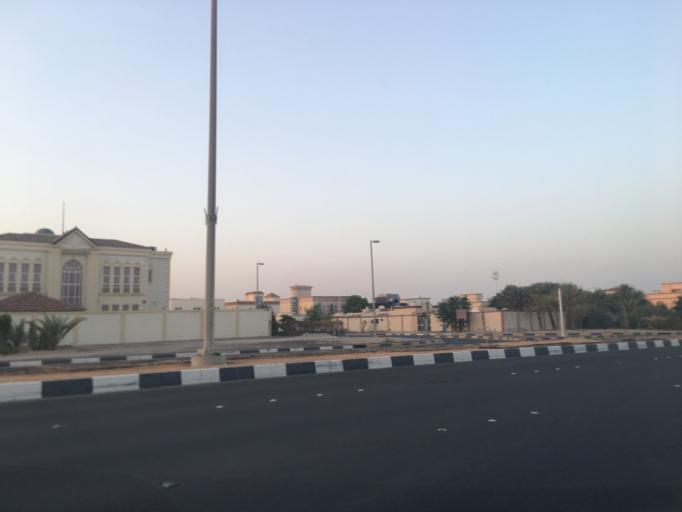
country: AE
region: Abu Dhabi
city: Abu Dhabi
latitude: 24.3047
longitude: 54.6374
